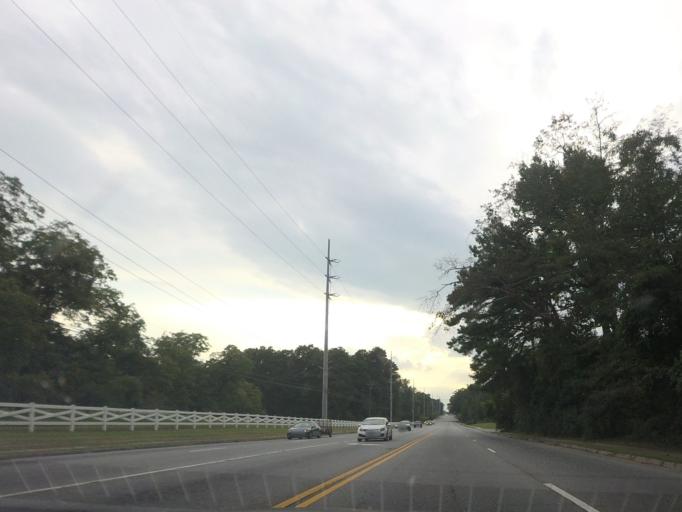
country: US
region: Georgia
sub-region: Bibb County
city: West Point
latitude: 32.8797
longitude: -83.7466
